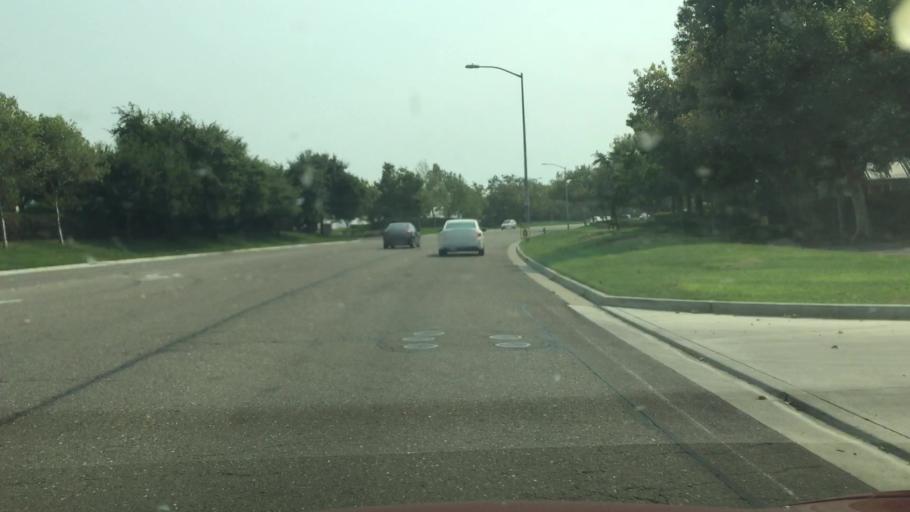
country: US
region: California
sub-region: San Joaquin County
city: Manteca
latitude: 37.7903
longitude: -121.1970
